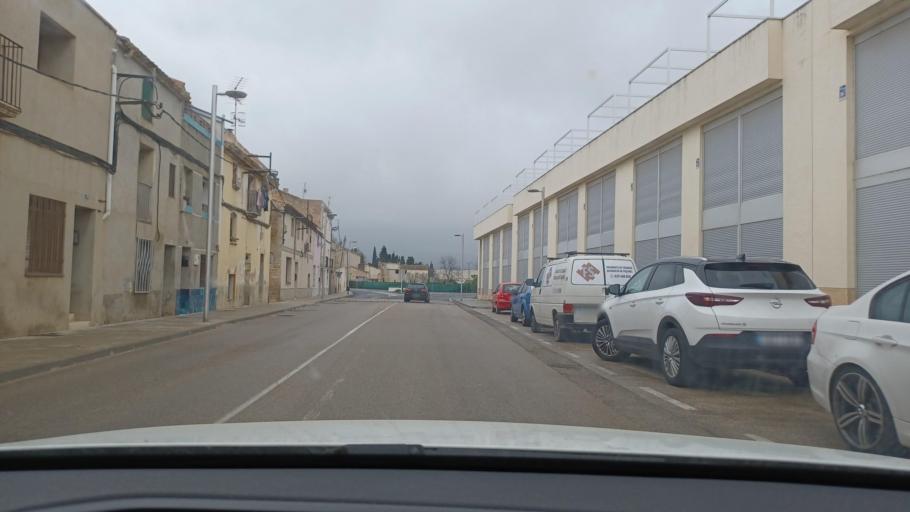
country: ES
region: Catalonia
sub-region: Provincia de Tarragona
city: Tortosa
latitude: 40.8089
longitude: 0.4986
